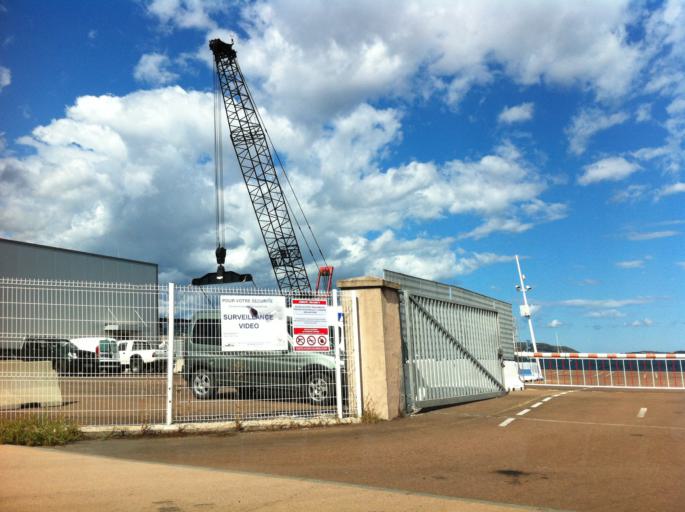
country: FR
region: Corsica
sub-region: Departement de la Corse-du-Sud
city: Porto-Vecchio
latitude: 41.5872
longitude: 9.2895
